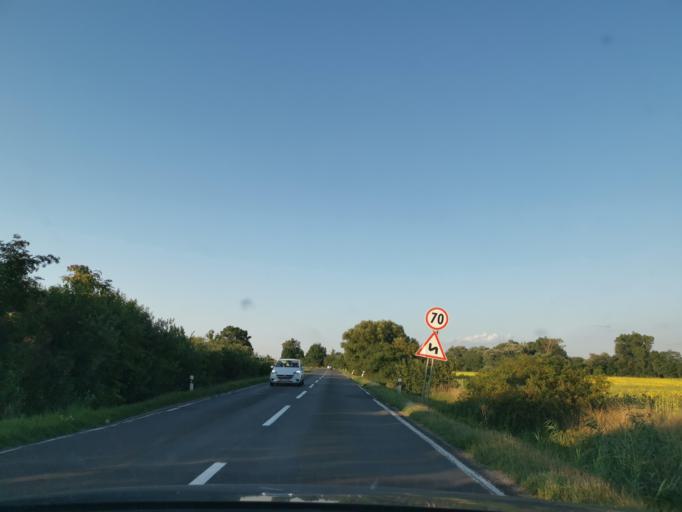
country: CZ
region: South Moravian
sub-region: Okres Breclav
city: Lanzhot
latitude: 48.6431
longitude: 17.0062
